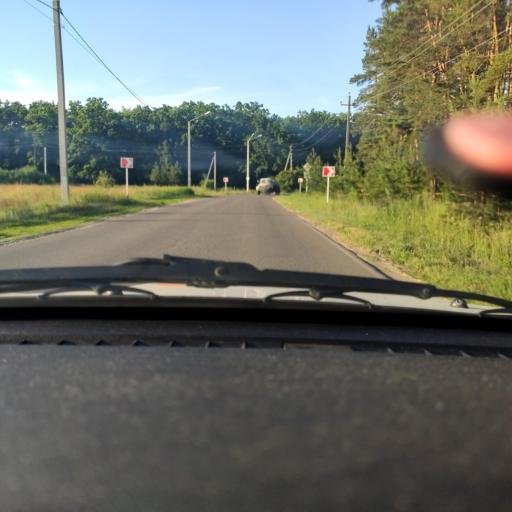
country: RU
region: Voronezj
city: Ramon'
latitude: 51.8947
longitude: 39.2760
